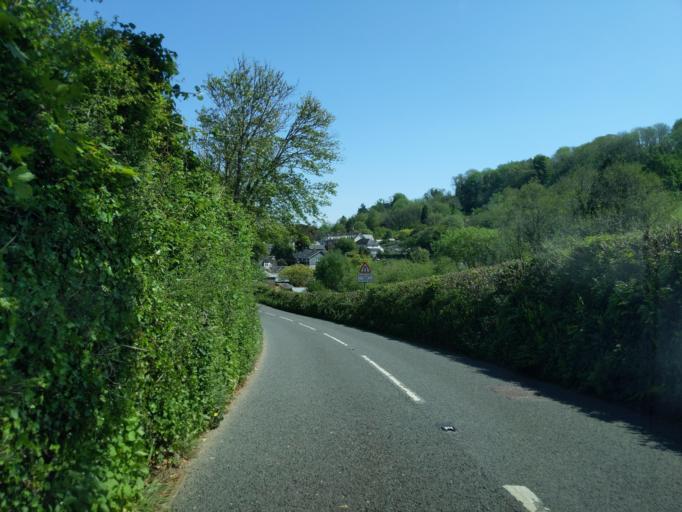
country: GB
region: England
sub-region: Cornwall
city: Pillaton
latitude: 50.3981
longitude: -4.3183
